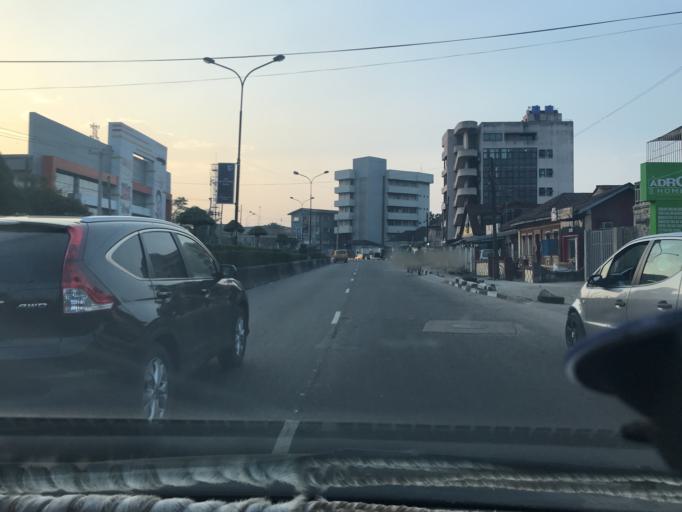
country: NG
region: Lagos
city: Makoko
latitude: 6.4985
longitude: 3.3786
